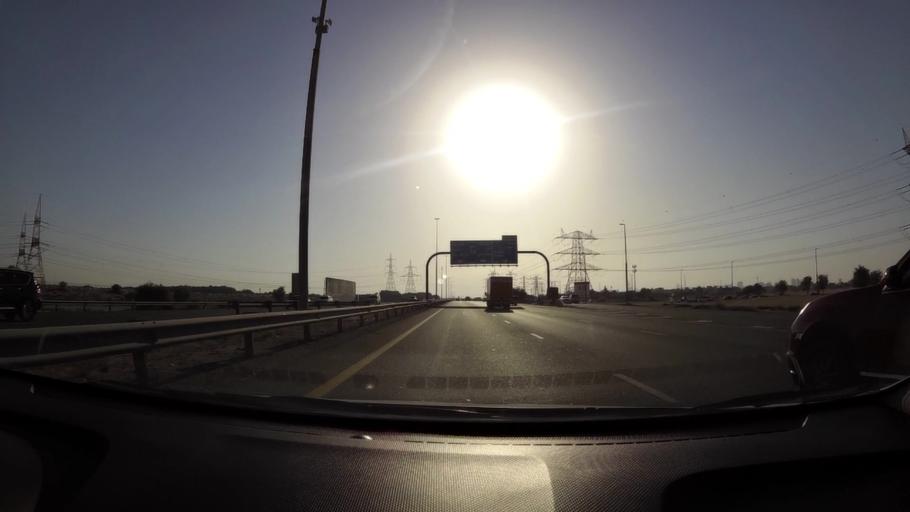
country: AE
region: Ajman
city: Ajman
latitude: 25.3578
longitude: 55.4968
